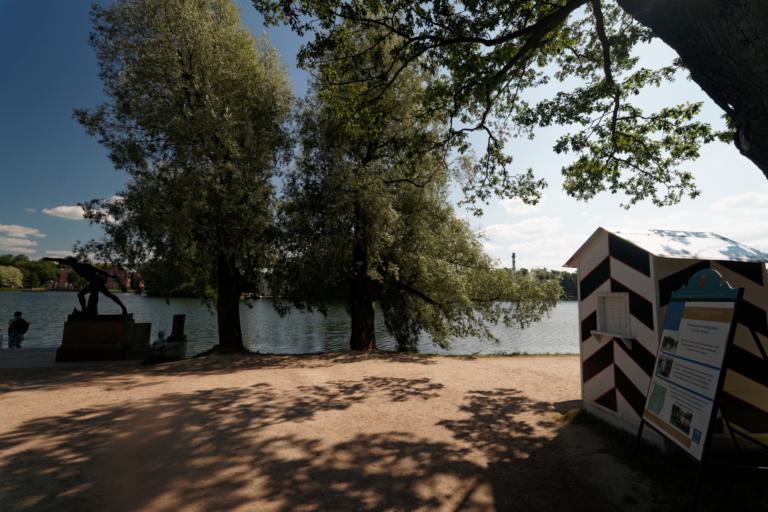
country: RU
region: St.-Petersburg
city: Pushkin
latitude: 59.7118
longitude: 30.3933
